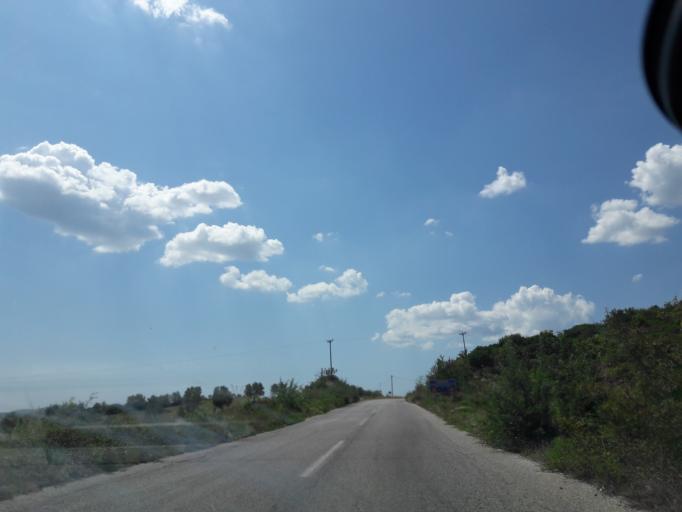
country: GR
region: Central Macedonia
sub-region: Nomos Chalkidikis
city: Ormylia
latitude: 40.3603
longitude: 23.5975
